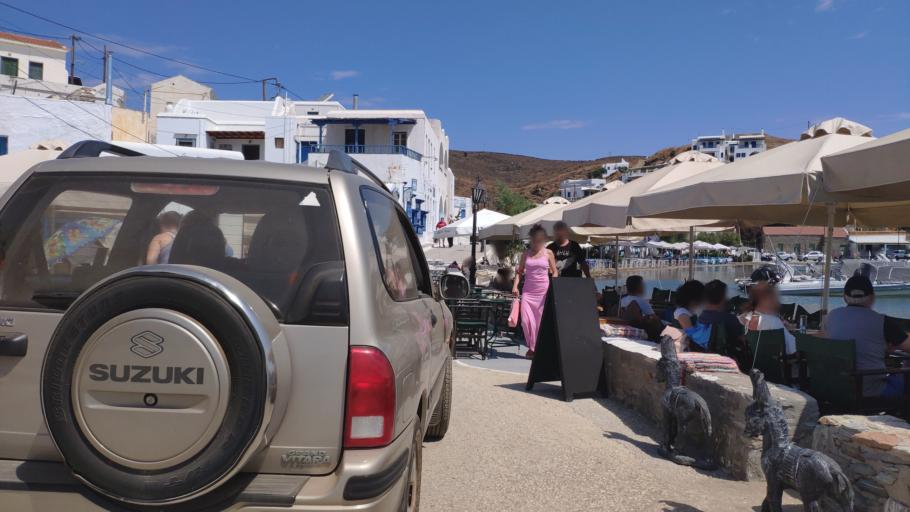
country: GR
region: South Aegean
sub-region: Nomos Kykladon
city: Kythnos
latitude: 37.4424
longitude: 24.4251
